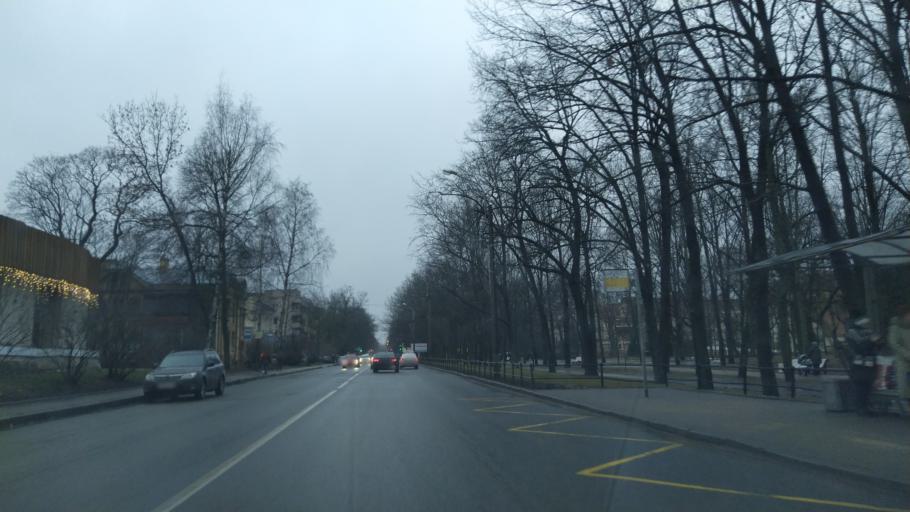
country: RU
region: St.-Petersburg
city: Pushkin
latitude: 59.7243
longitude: 30.4090
